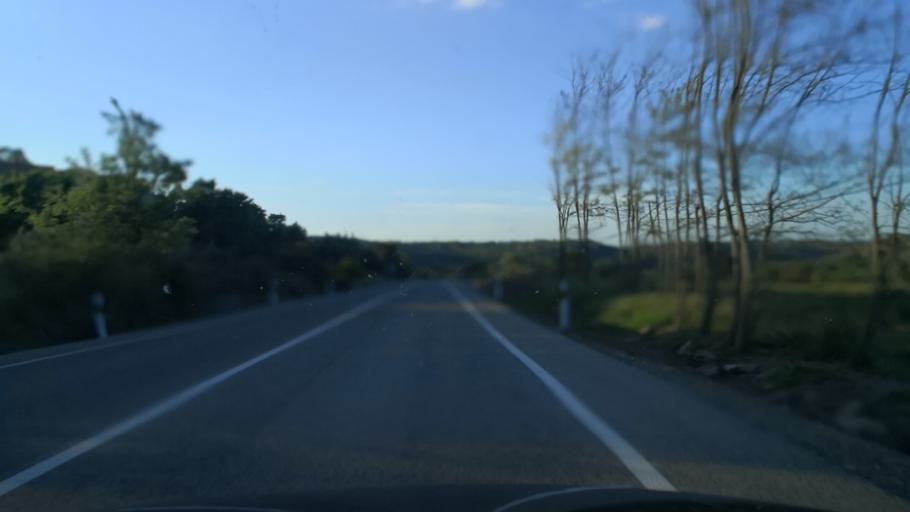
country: PT
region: Portalegre
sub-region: Portalegre
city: Sao Juliao
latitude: 39.3555
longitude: -7.2749
